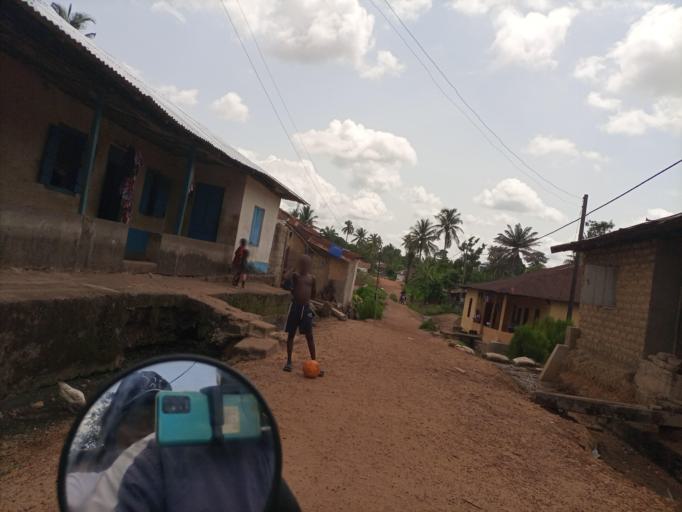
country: SL
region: Southern Province
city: Bo
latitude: 7.9576
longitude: -11.7360
